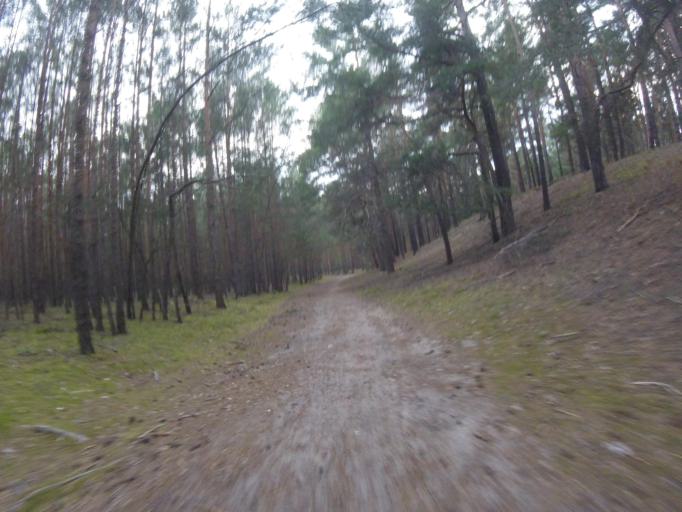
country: DE
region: Brandenburg
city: Gross Koris
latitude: 52.1564
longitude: 13.6856
